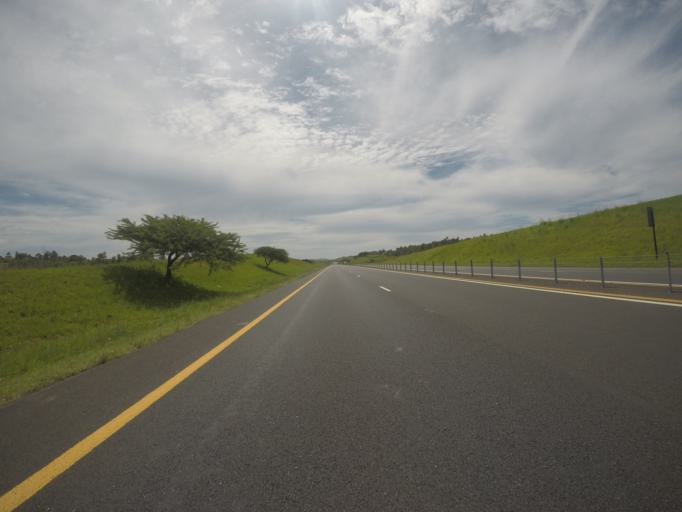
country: ZA
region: KwaZulu-Natal
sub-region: iLembe District Municipality
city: Mandeni
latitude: -29.1818
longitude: 31.4909
